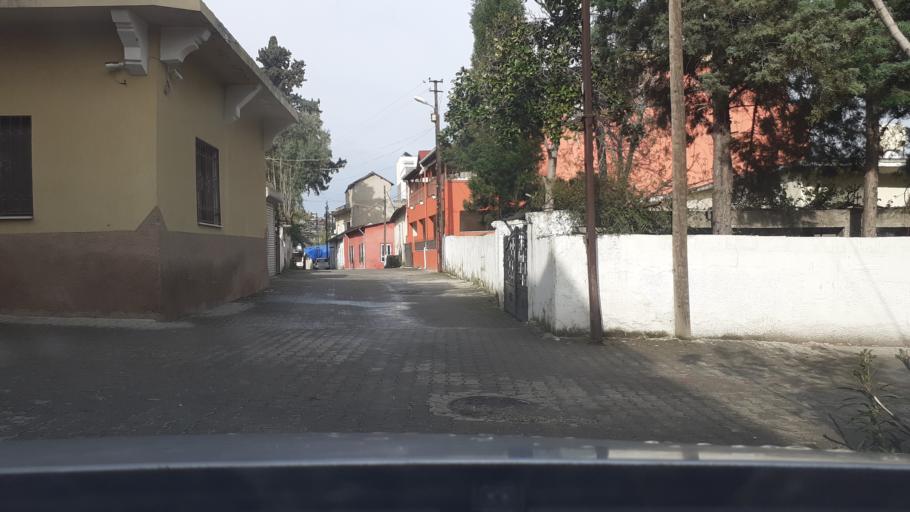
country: TR
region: Hatay
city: Kirikhan
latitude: 36.5000
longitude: 36.3516
